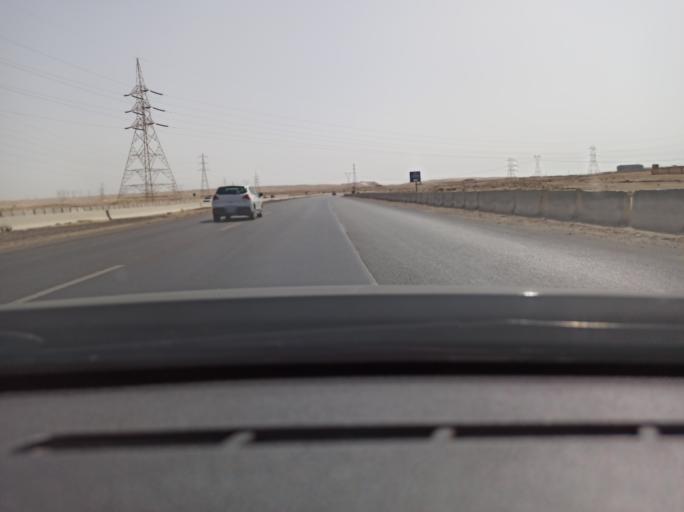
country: EG
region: Muhafazat al Qahirah
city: Halwan
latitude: 29.7665
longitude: 31.3933
